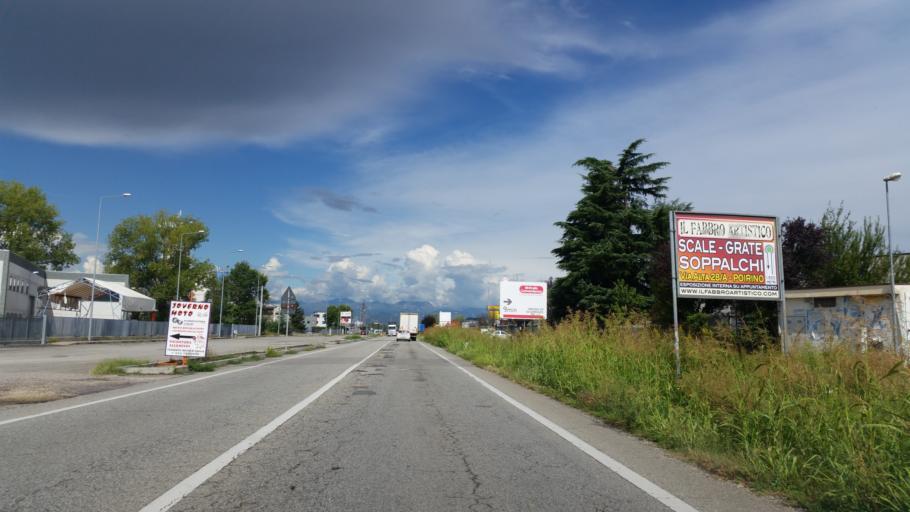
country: IT
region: Piedmont
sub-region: Provincia di Torino
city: Santena
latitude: 44.9529
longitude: 7.7954
